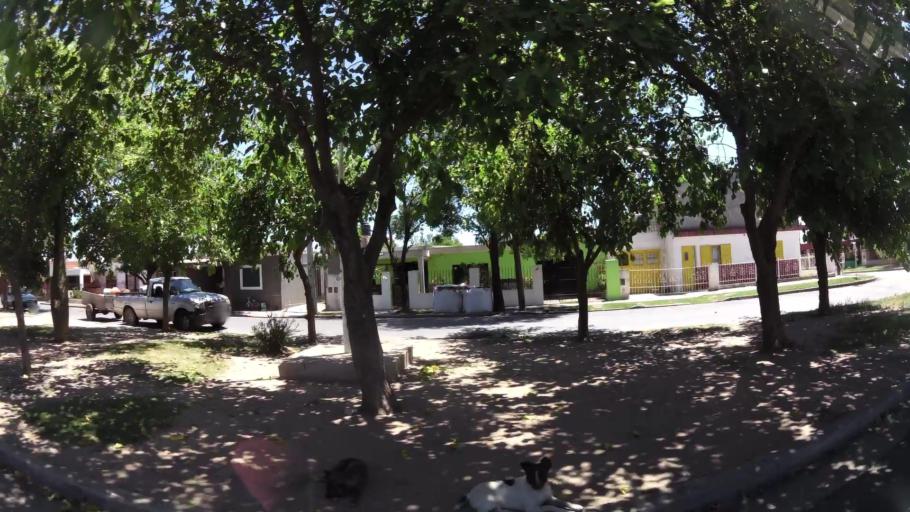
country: AR
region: Cordoba
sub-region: Departamento de Capital
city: Cordoba
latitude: -31.4220
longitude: -64.1215
